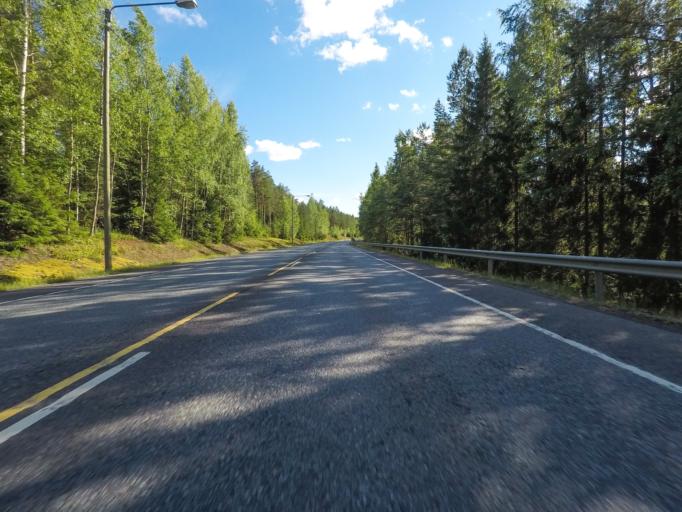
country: FI
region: Uusimaa
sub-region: Helsinki
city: Vihti
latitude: 60.3349
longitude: 24.2892
